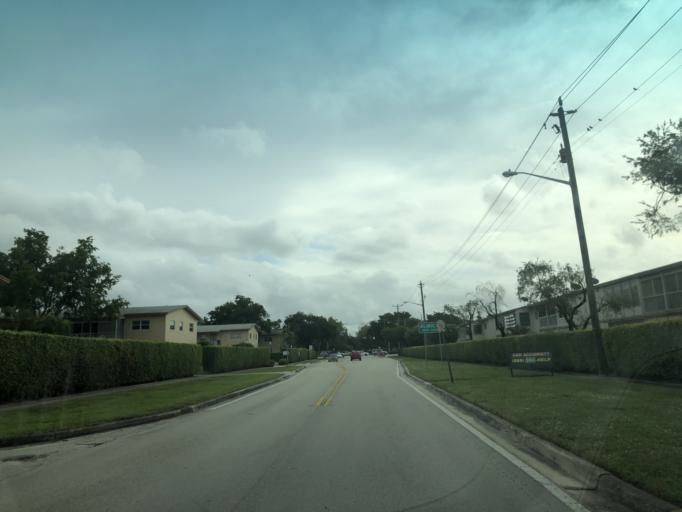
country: US
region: Florida
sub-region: Broward County
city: North Lauderdale
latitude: 26.2371
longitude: -80.2268
